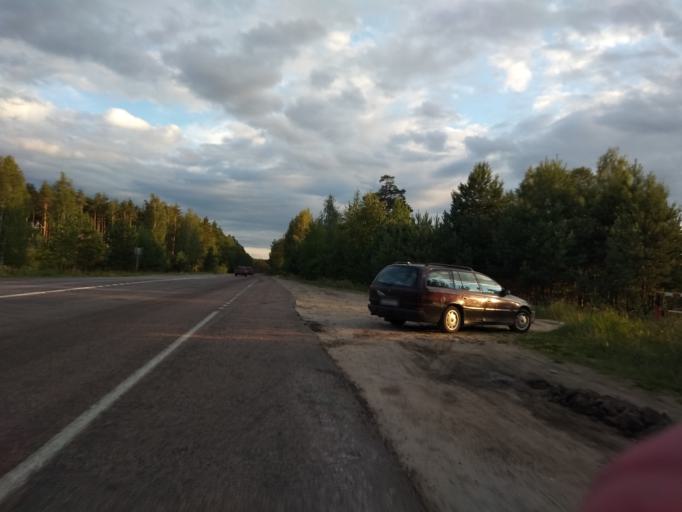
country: RU
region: Moskovskaya
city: Misheronskiy
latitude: 55.6337
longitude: 39.7459
